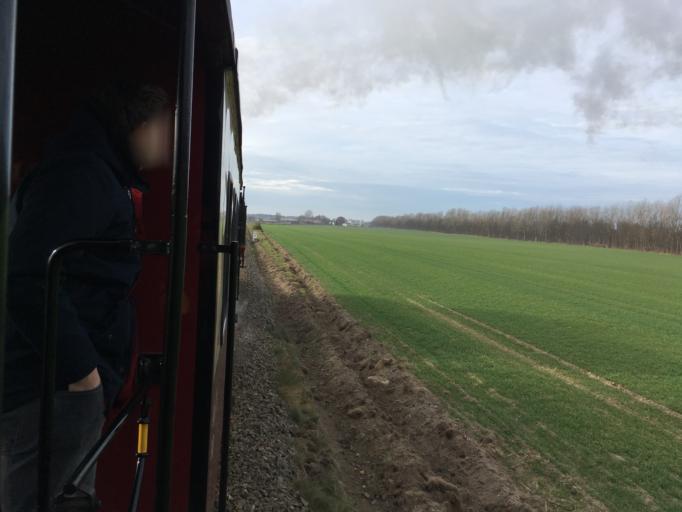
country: DE
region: Mecklenburg-Vorpommern
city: Ostseebad Kuhlungsborn
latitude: 54.1452
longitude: 11.7901
